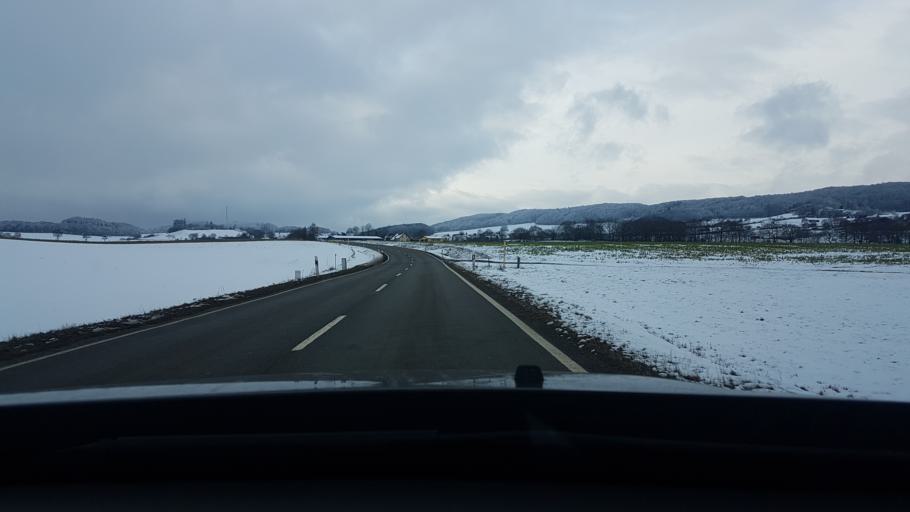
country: DE
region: North Rhine-Westphalia
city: Marsberg
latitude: 51.3599
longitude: 8.7868
